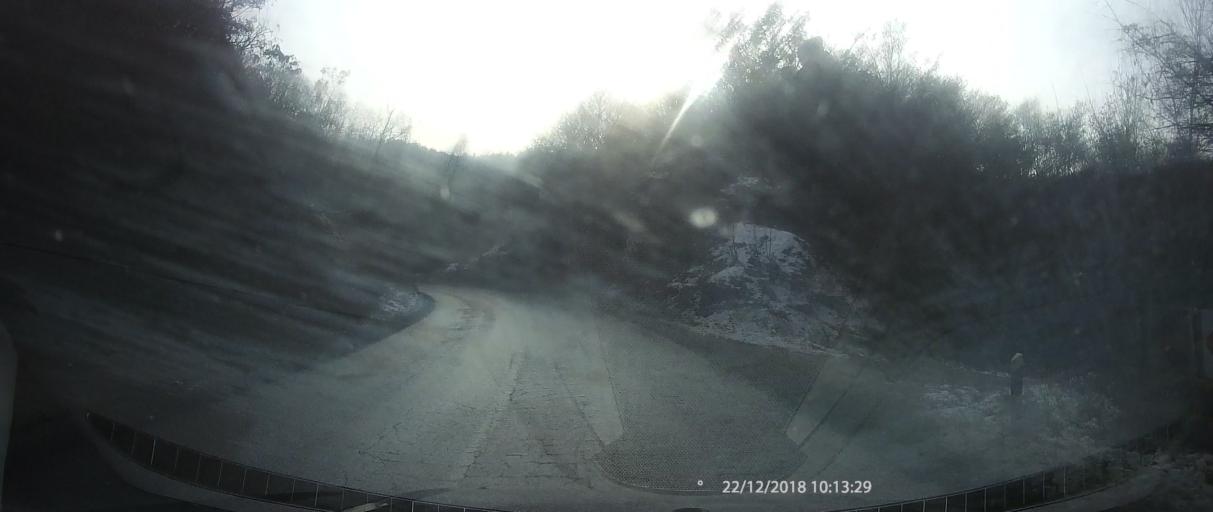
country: MK
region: Kratovo
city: Kratovo
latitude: 42.1728
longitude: 22.2242
